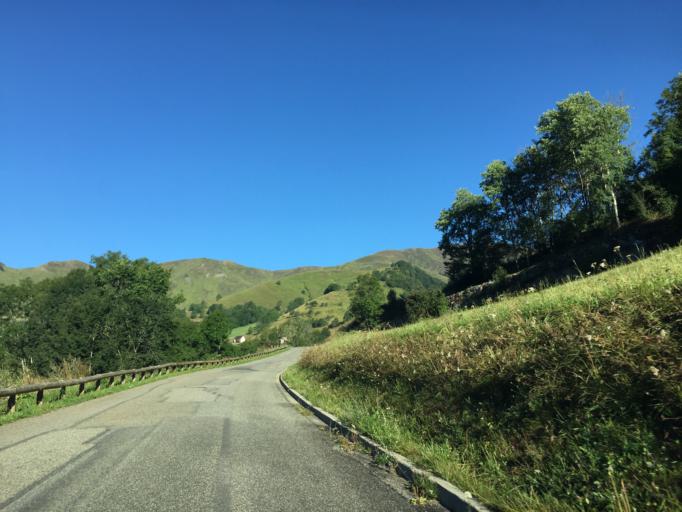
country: FR
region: Midi-Pyrenees
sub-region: Departement de la Haute-Garonne
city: Bagneres-de-Luchon
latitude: 42.8112
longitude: 0.4944
